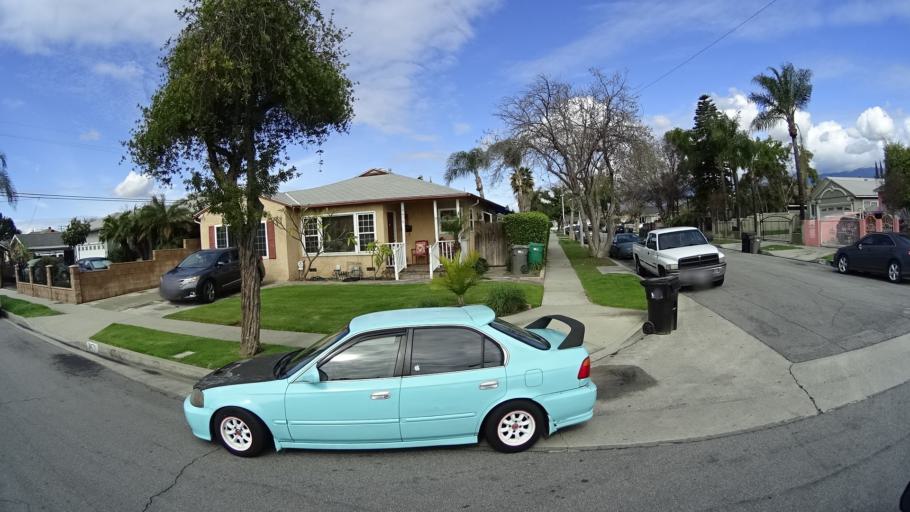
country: US
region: California
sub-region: Los Angeles County
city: Baldwin Park
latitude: 34.0775
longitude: -117.9643
